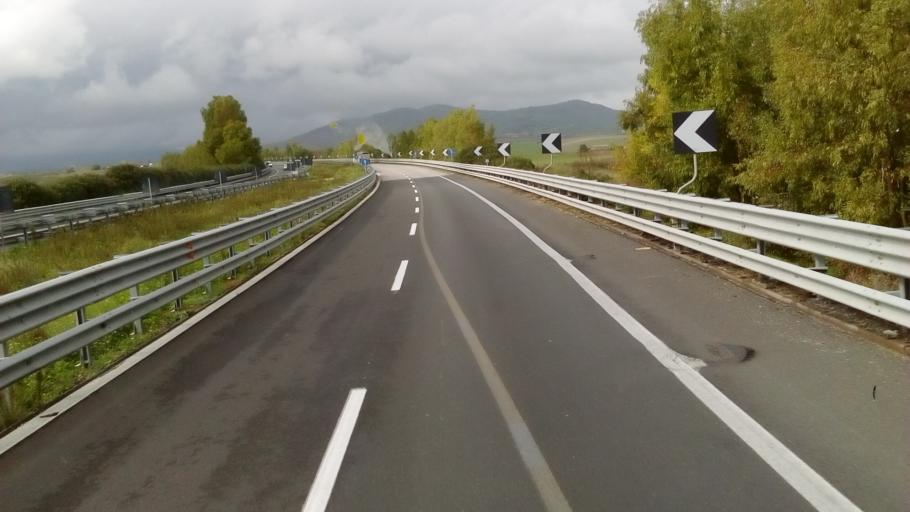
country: IT
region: Sicily
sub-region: Enna
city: Assoro
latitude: 37.5770
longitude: 14.4356
